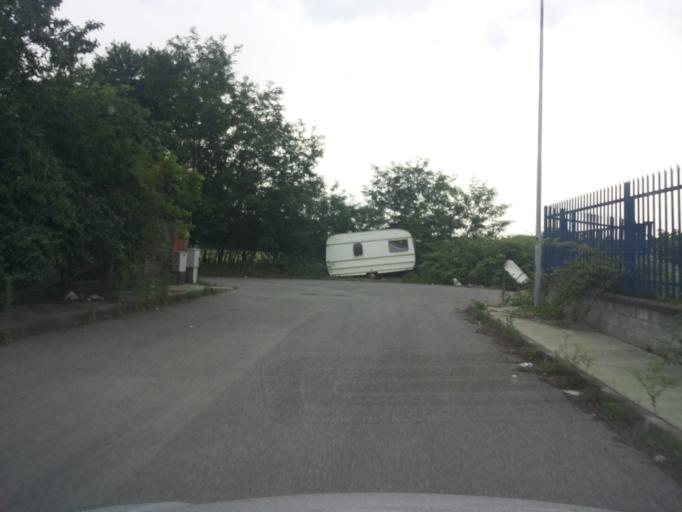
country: IT
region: Piedmont
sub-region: Provincia di Biella
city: Cavaglia
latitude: 45.3869
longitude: 8.1263
